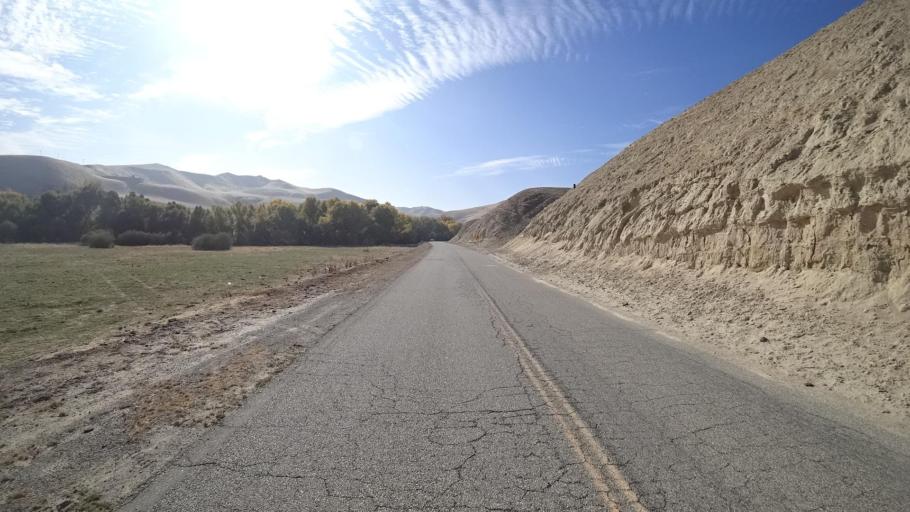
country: US
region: California
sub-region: Kern County
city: Oildale
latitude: 35.5176
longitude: -118.9214
